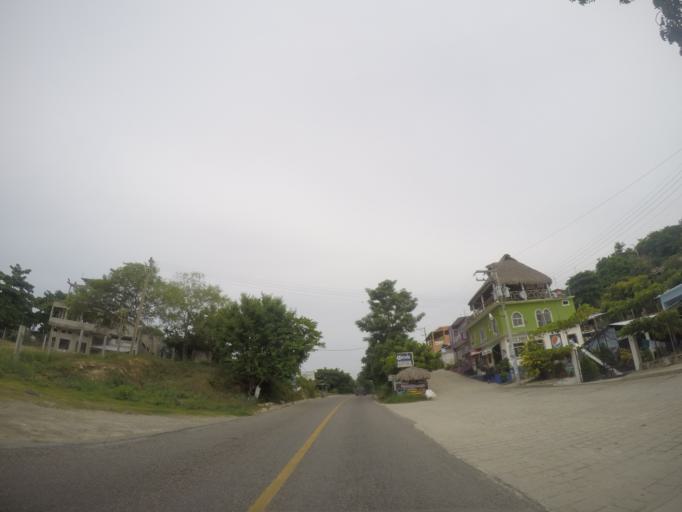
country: MX
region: Oaxaca
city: San Pedro Mixtepec
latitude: 15.9467
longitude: -97.1858
